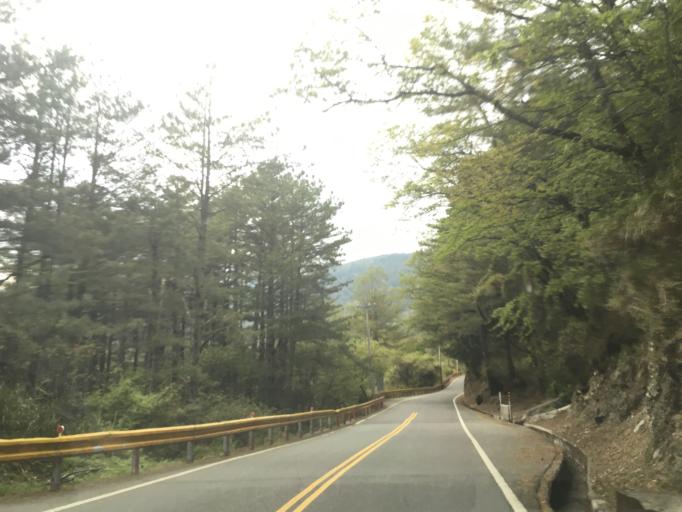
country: TW
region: Taiwan
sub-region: Hualien
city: Hualian
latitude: 24.1865
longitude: 121.3376
